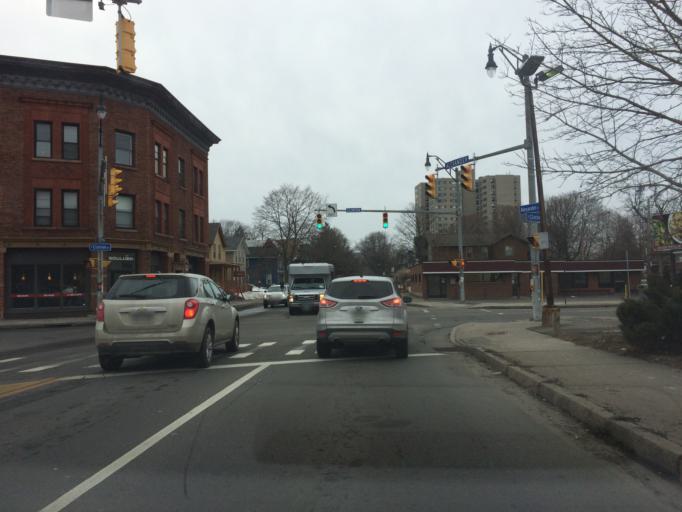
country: US
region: New York
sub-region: Monroe County
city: Rochester
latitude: 43.1462
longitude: -77.6019
